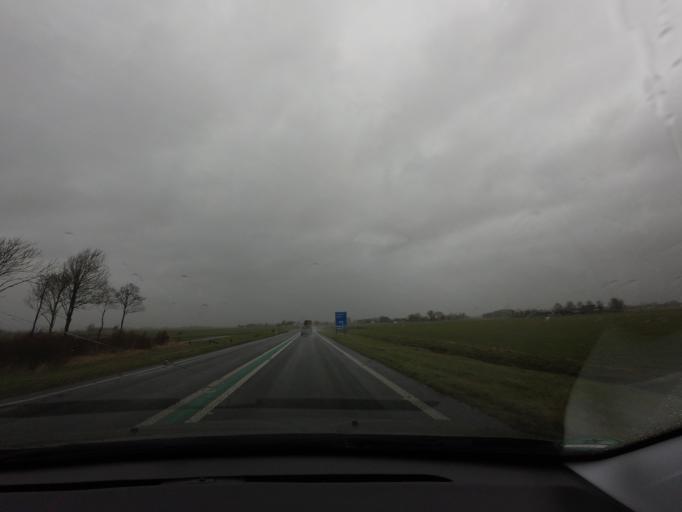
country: NL
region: Friesland
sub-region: Sudwest Fryslan
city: Bolsward
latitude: 53.0885
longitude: 5.5278
